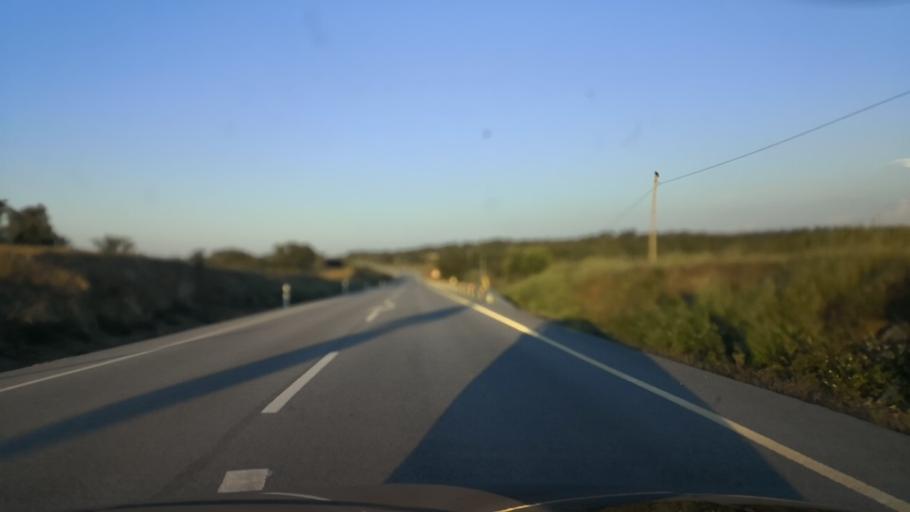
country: ES
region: Extremadura
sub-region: Provincia de Caceres
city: Salorino
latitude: 39.5133
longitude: -7.0868
